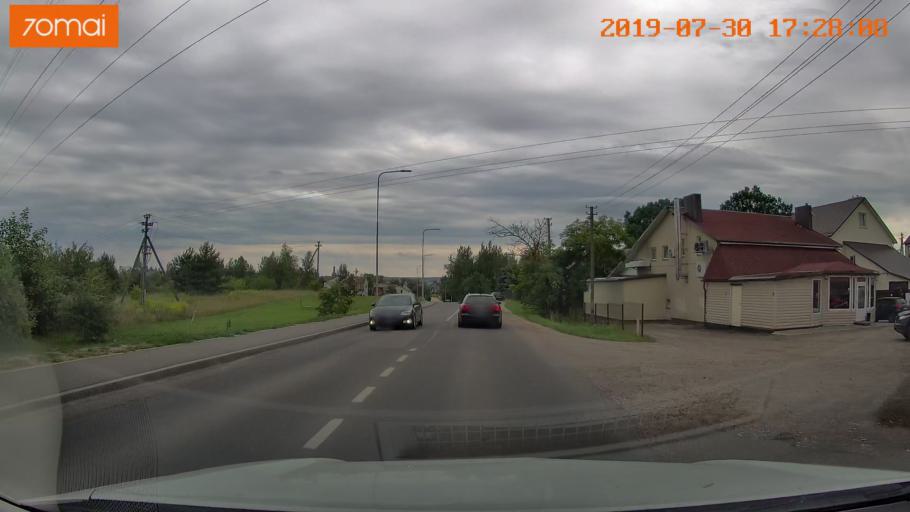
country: LT
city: Skaidiskes
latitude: 54.7083
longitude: 25.4177
